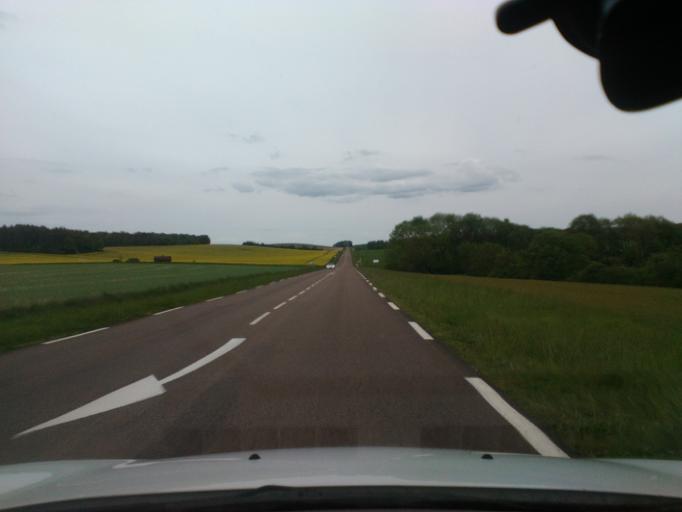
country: FR
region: Champagne-Ardenne
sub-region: Departement de l'Aube
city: Bar-sur-Aube
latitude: 48.2228
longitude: 4.7631
